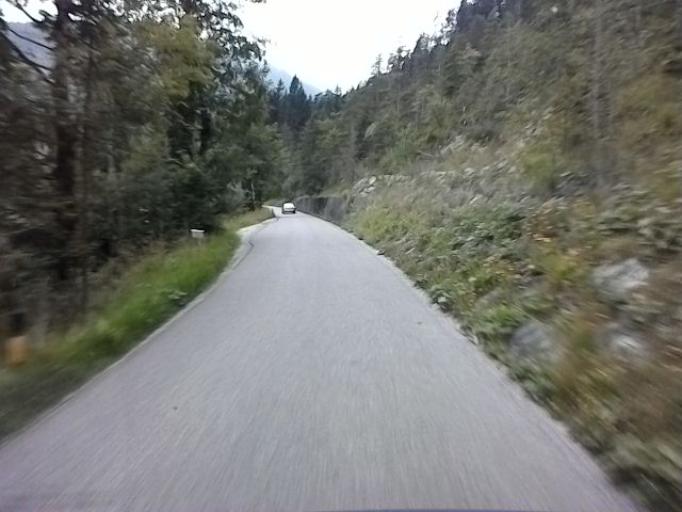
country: DE
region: Bavaria
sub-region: Upper Bavaria
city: Jachenau
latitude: 47.5572
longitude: 11.4300
